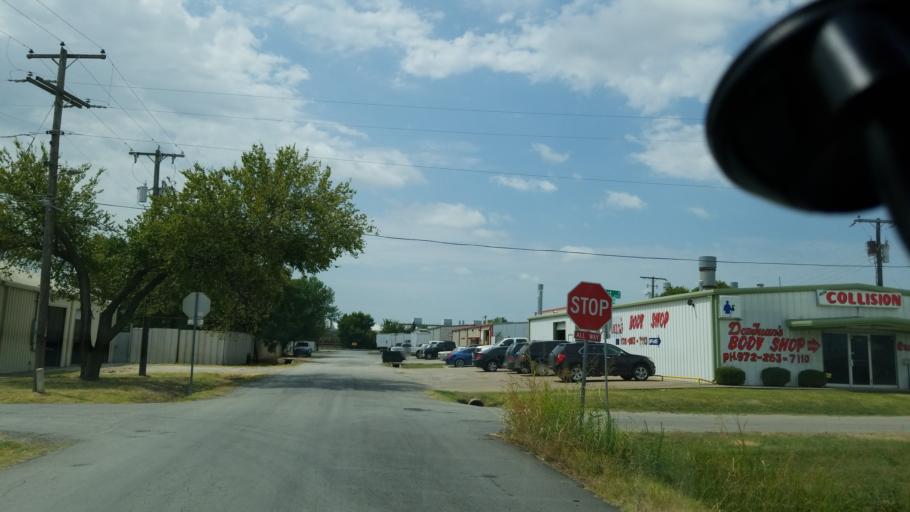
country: US
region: Texas
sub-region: Dallas County
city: Grand Prairie
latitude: 32.7480
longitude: -96.9771
